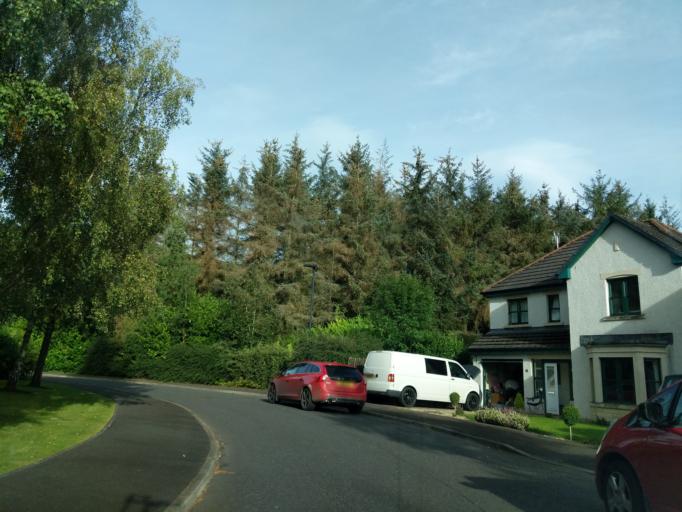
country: GB
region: Scotland
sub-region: The Scottish Borders
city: Innerleithen
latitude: 55.6367
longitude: -3.1042
